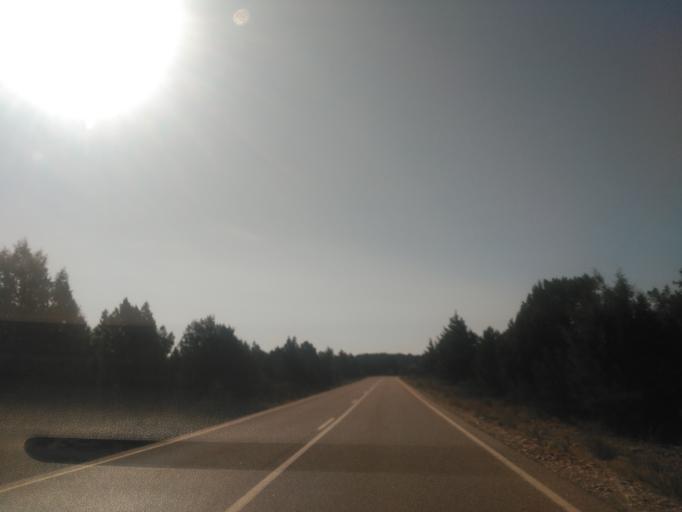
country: ES
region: Castille and Leon
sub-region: Provincia de Soria
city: Ucero
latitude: 41.7346
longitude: -3.0428
